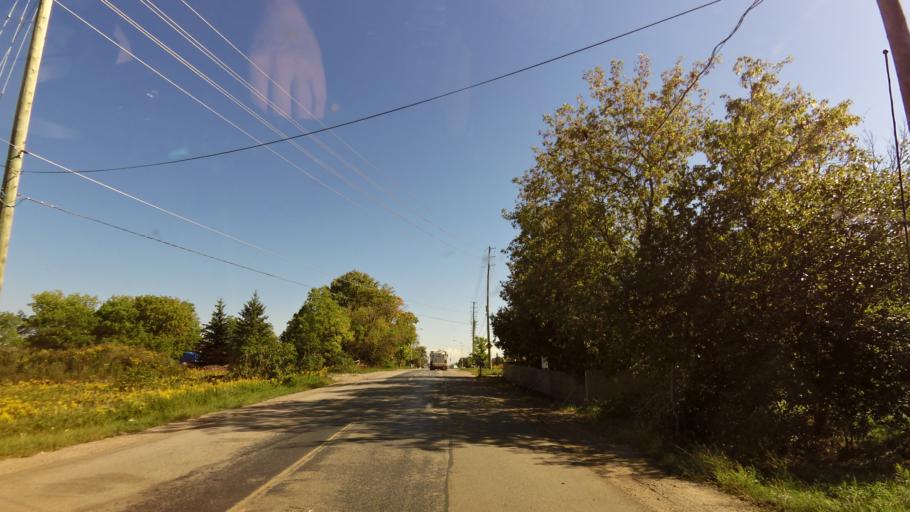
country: CA
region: Ontario
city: Oakville
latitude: 43.4810
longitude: -79.7316
